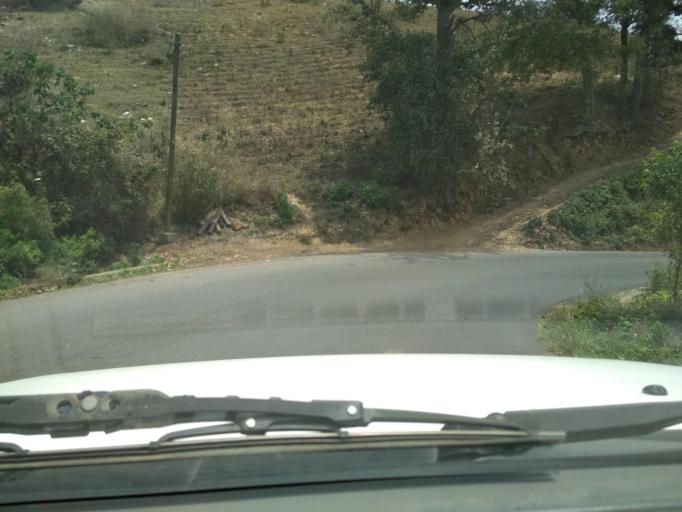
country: MX
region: Veracruz
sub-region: Acultzingo
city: Acatla
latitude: 18.7520
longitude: -97.1992
